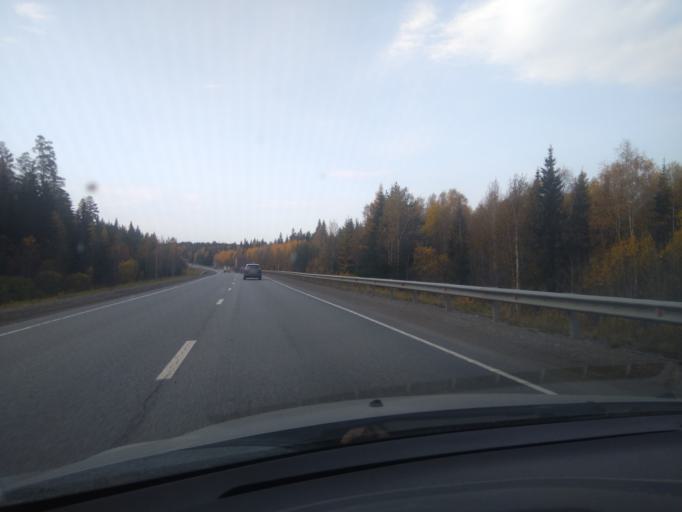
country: RU
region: Sverdlovsk
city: Druzhinino
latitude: 56.8250
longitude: 59.5817
